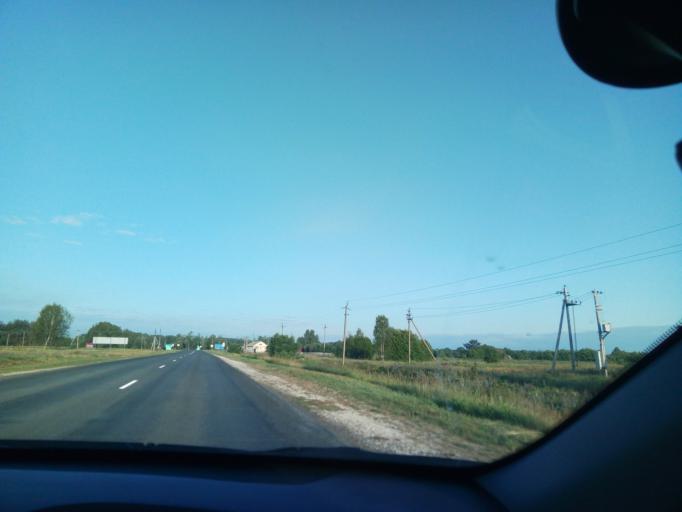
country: RU
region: Nizjnij Novgorod
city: Voznesenskoye
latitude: 54.8571
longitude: 42.8989
